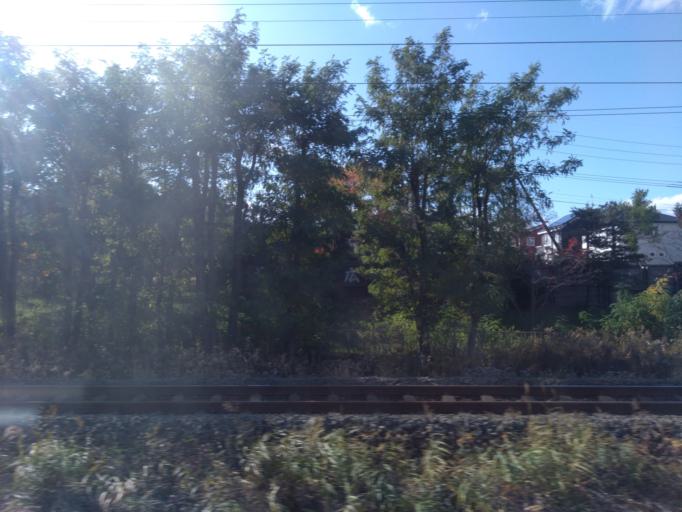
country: JP
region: Hokkaido
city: Kitahiroshima
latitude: 42.9698
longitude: 141.5658
